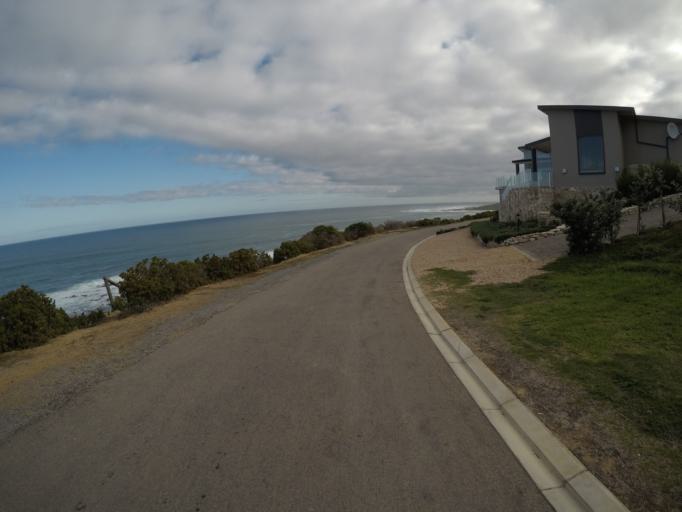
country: ZA
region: Western Cape
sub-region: Eden District Municipality
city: Riversdale
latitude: -34.4314
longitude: 21.3271
